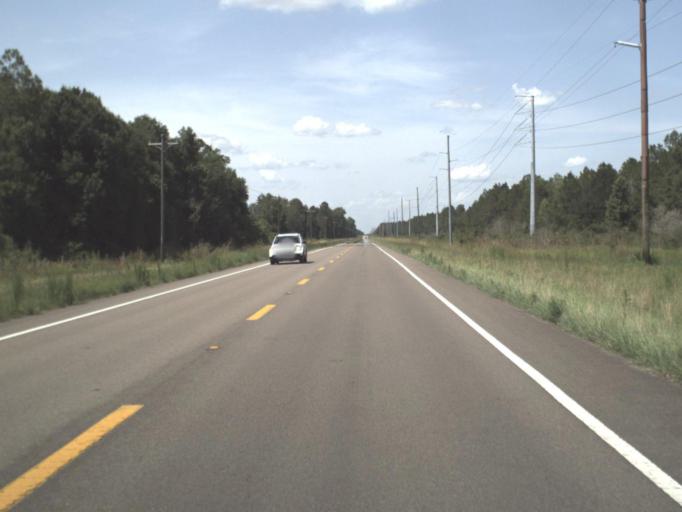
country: US
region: Florida
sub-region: Gilchrist County
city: Trenton
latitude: 29.6459
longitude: -82.7904
